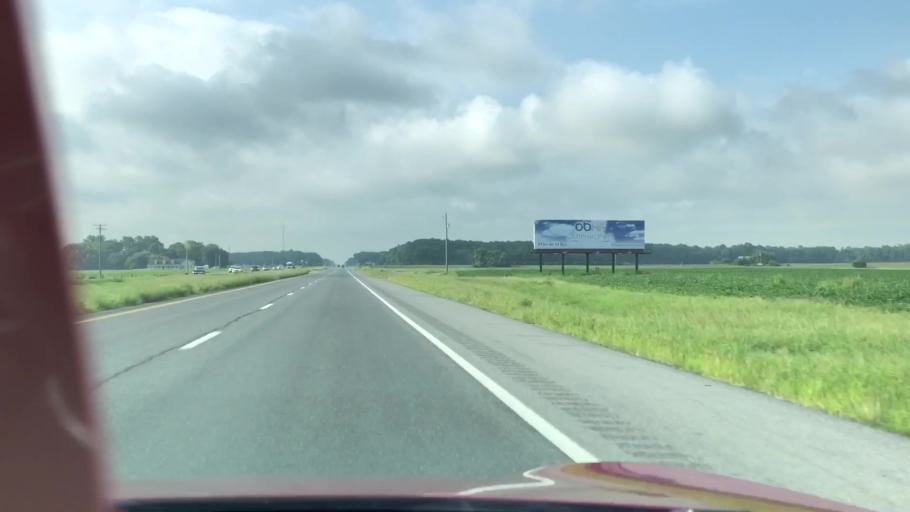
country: US
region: Delaware
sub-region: Sussex County
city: Laurel
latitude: 38.5376
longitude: -75.5587
